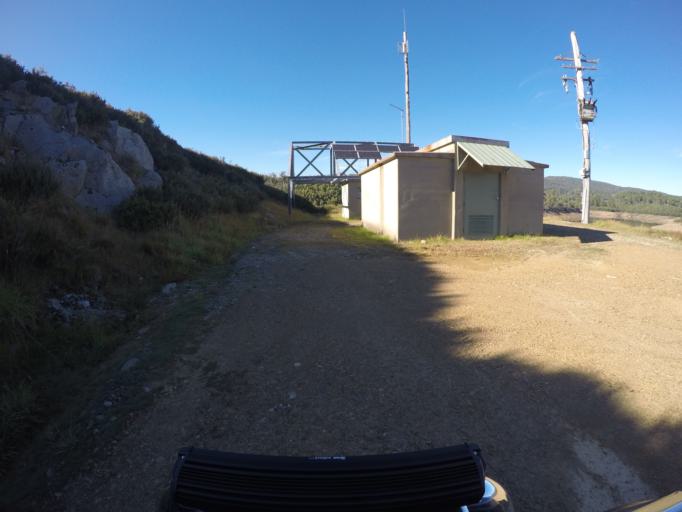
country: AU
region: New South Wales
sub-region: Snowy River
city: Jindabyne
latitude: -36.0545
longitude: 148.2783
